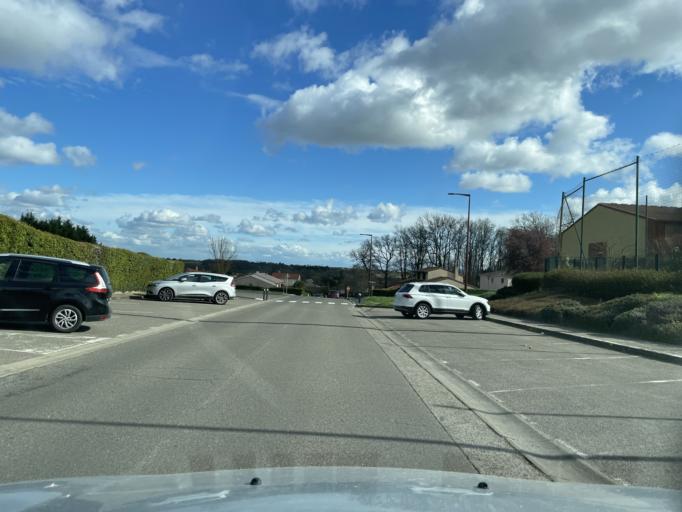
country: FR
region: Midi-Pyrenees
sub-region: Departement de la Haute-Garonne
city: Pibrac
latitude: 43.6153
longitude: 1.2783
